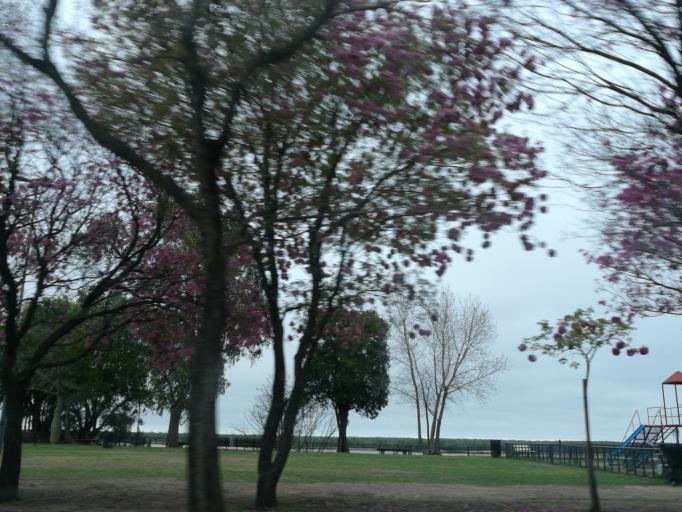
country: AR
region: Santa Fe
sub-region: Departamento de Rosario
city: Rosario
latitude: -32.9292
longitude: -60.6533
